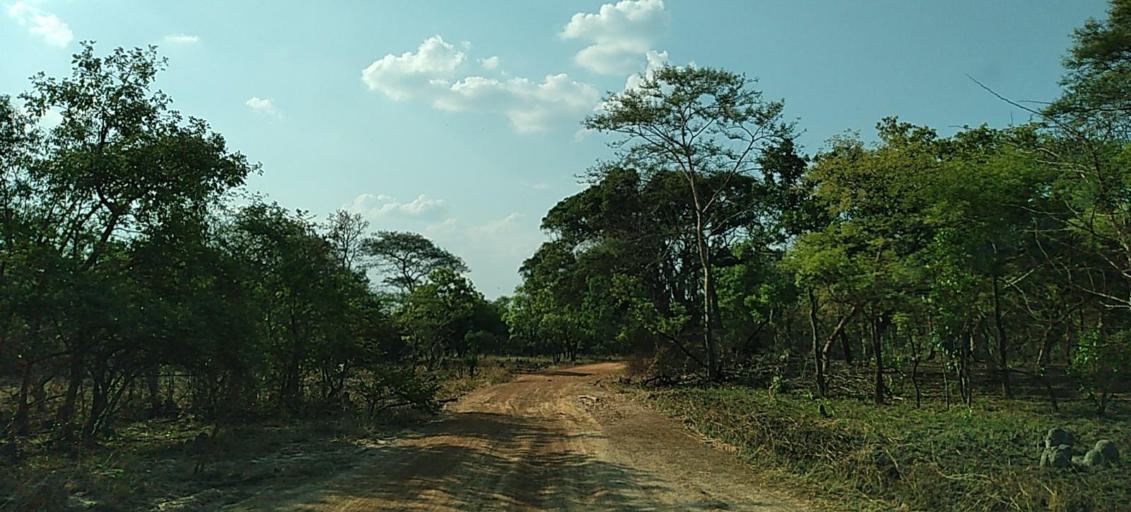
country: ZM
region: Copperbelt
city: Mpongwe
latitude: -13.4392
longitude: 28.0603
